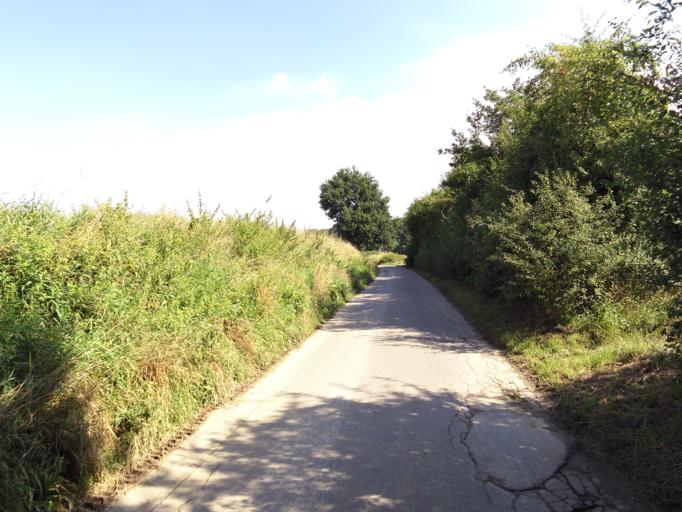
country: NL
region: Limburg
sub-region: Gemeente Kerkrade
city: Kerkrade
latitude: 50.8409
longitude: 6.0555
